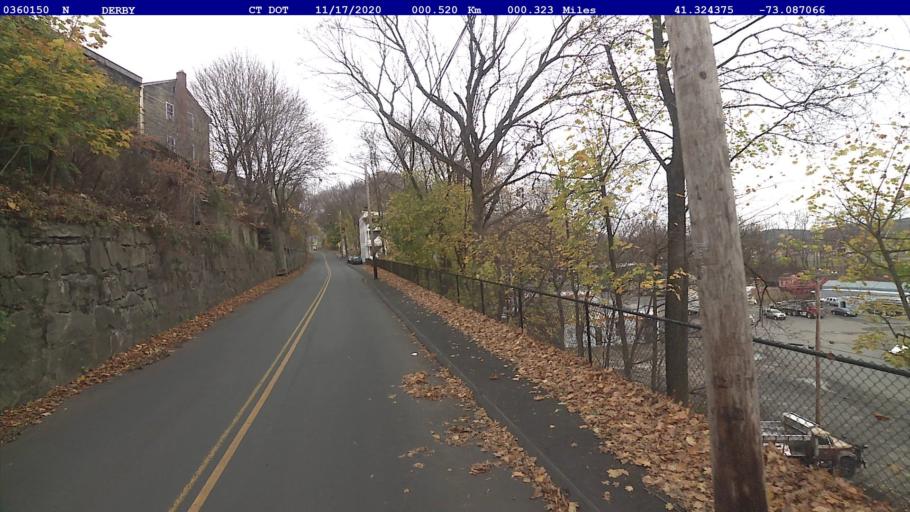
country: US
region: Connecticut
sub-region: New Haven County
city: Derby
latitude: 41.3244
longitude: -73.0871
